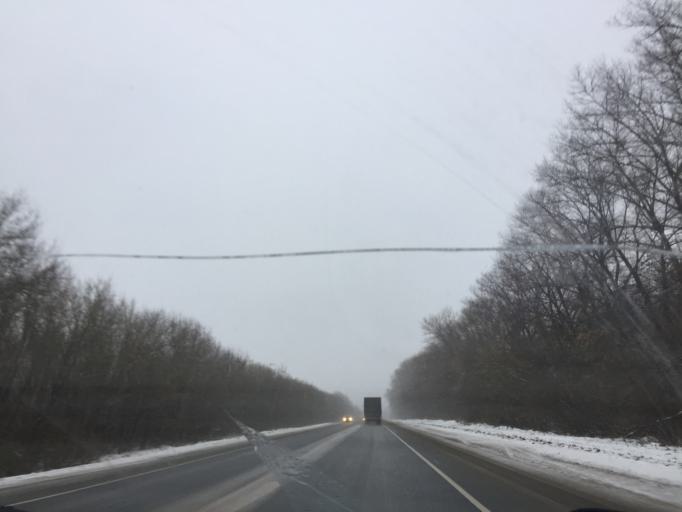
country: RU
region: Tula
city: Plavsk
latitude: 53.7587
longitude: 37.3360
